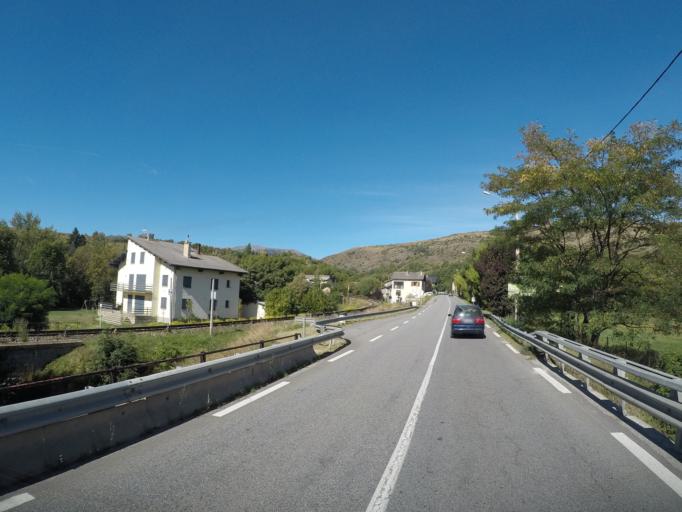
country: FR
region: Languedoc-Roussillon
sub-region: Departement des Pyrenees-Orientales
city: la Guingueta d'Ix
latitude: 42.4600
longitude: 1.9398
